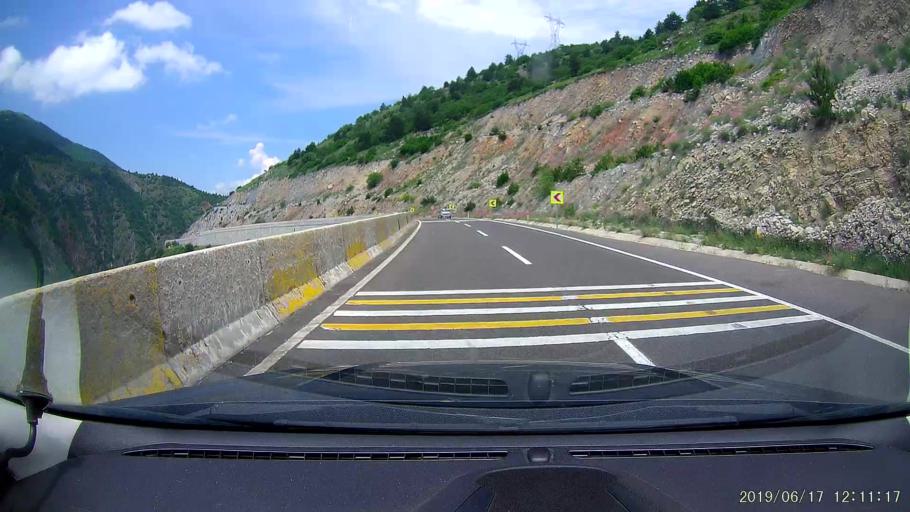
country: TR
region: Karabuk
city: Gozyeri
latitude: 40.8457
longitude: 32.6515
